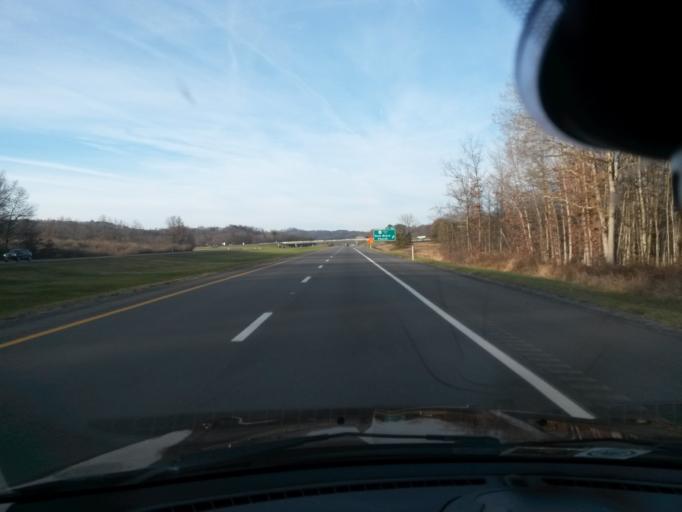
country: US
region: West Virginia
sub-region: Greenbrier County
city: Rainelle
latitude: 37.9057
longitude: -80.6264
